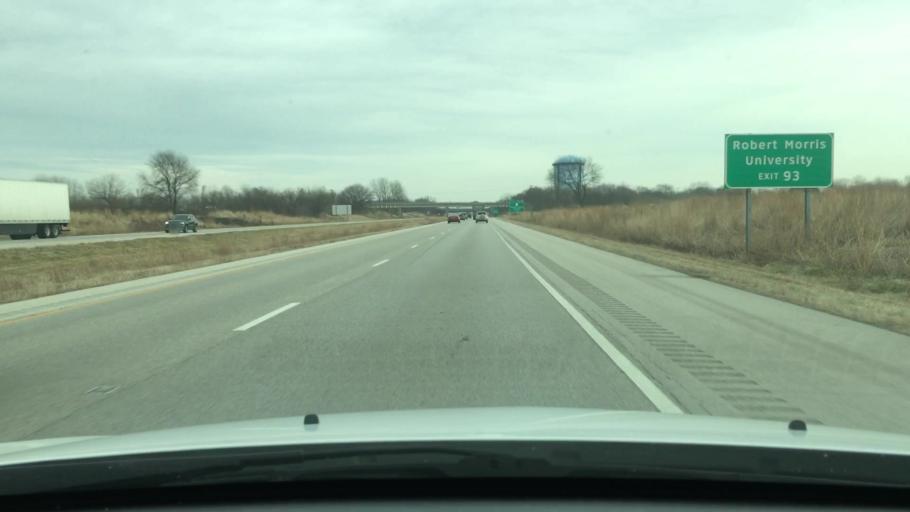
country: US
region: Illinois
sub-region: Sangamon County
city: Jerome
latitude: 39.7482
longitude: -89.7246
